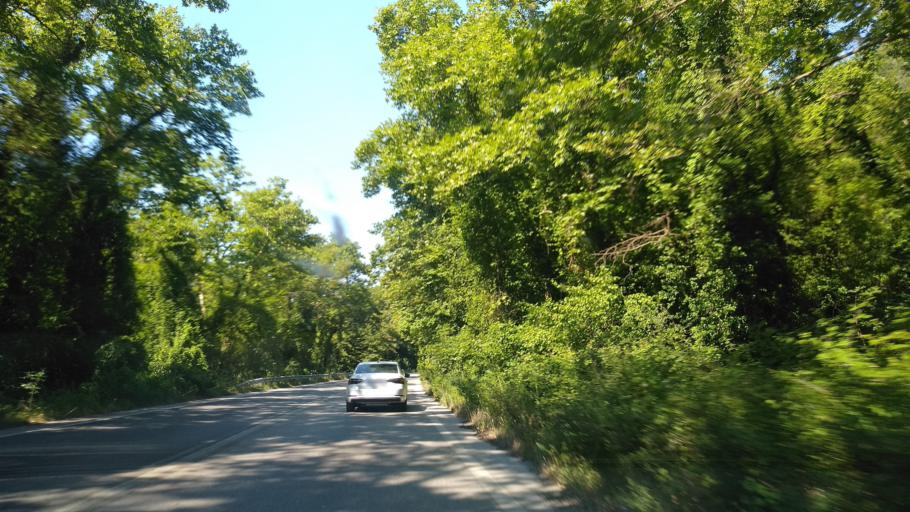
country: GR
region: Central Macedonia
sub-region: Nomos Thessalonikis
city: Stavros
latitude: 40.6604
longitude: 23.6341
